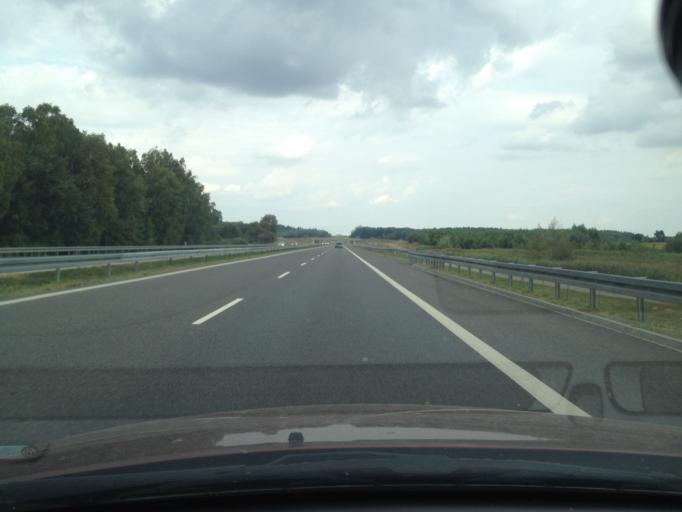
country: PL
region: West Pomeranian Voivodeship
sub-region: Powiat mysliborski
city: Mysliborz
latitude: 53.0002
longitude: 14.8622
